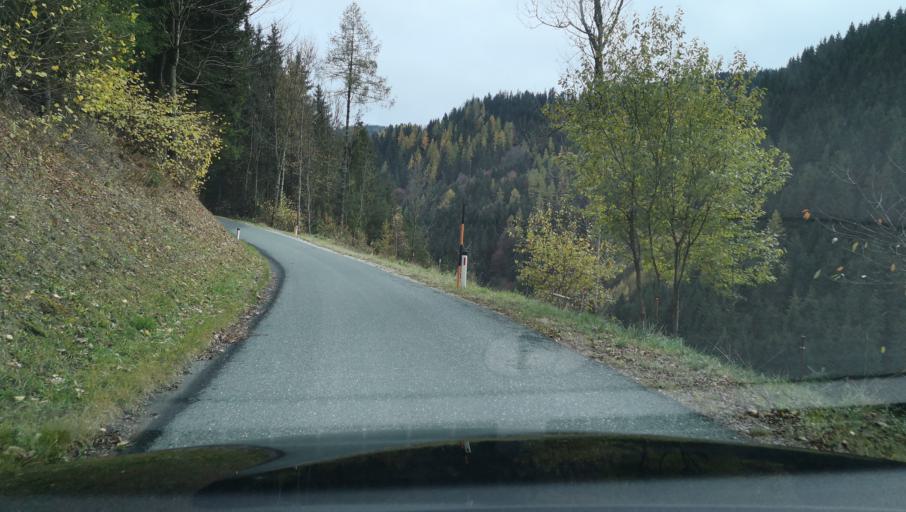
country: AT
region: Styria
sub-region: Politischer Bezirk Weiz
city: Birkfeld
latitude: 47.3688
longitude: 15.6302
